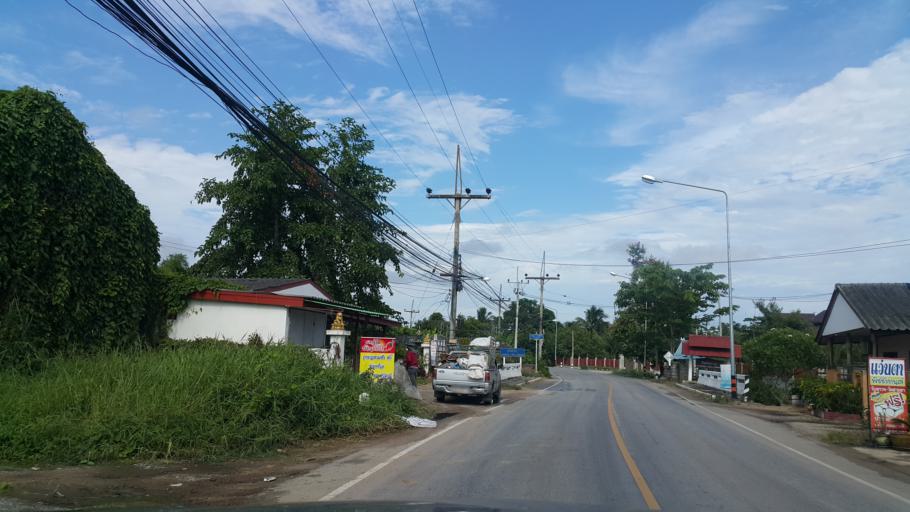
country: TH
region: Chiang Rai
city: Wiang Chai
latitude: 19.9182
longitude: 99.8897
